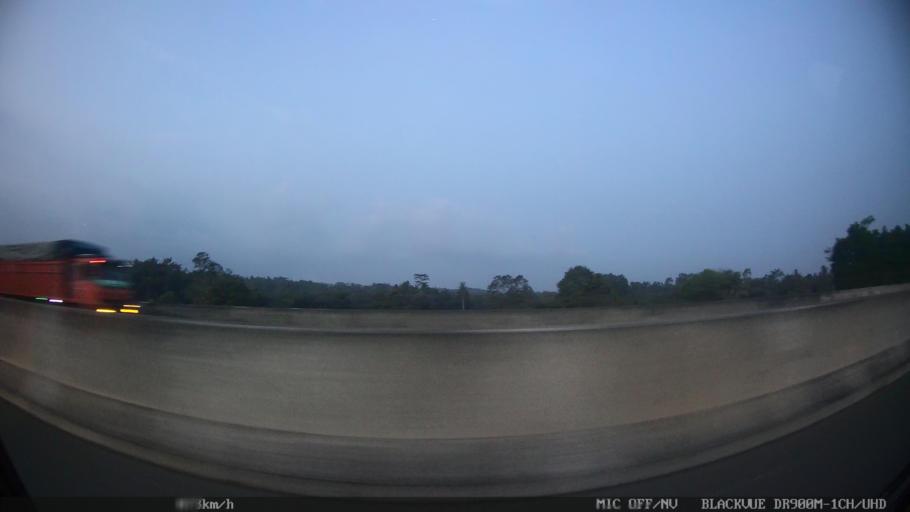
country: ID
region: Lampung
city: Sidorejo
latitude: -5.5658
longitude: 105.5346
